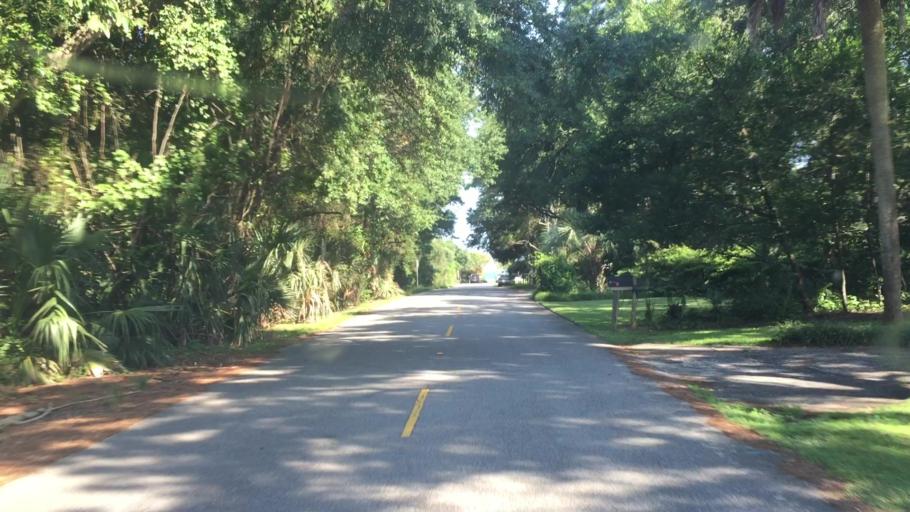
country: US
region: South Carolina
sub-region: Horry County
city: Myrtle Beach
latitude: 33.7484
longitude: -78.8100
